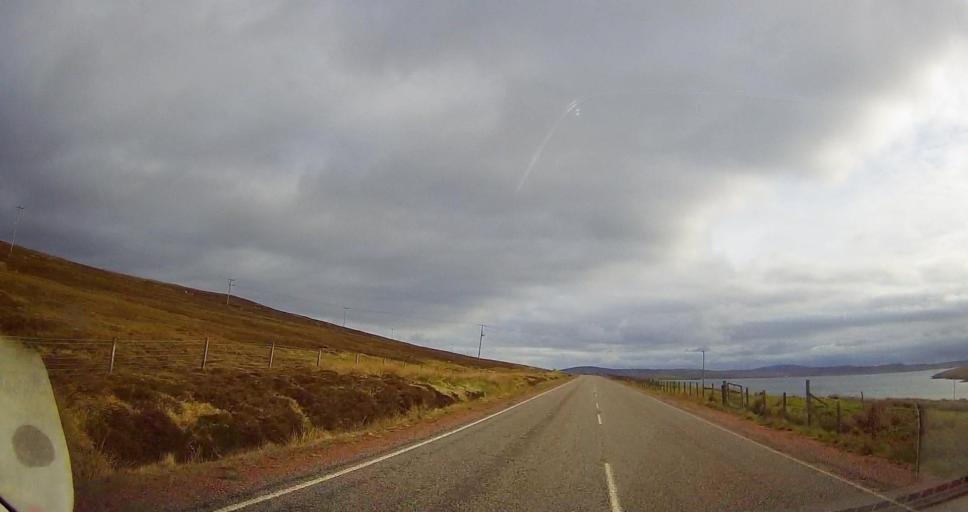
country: GB
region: Scotland
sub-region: Shetland Islands
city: Lerwick
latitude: 60.4556
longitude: -1.2120
